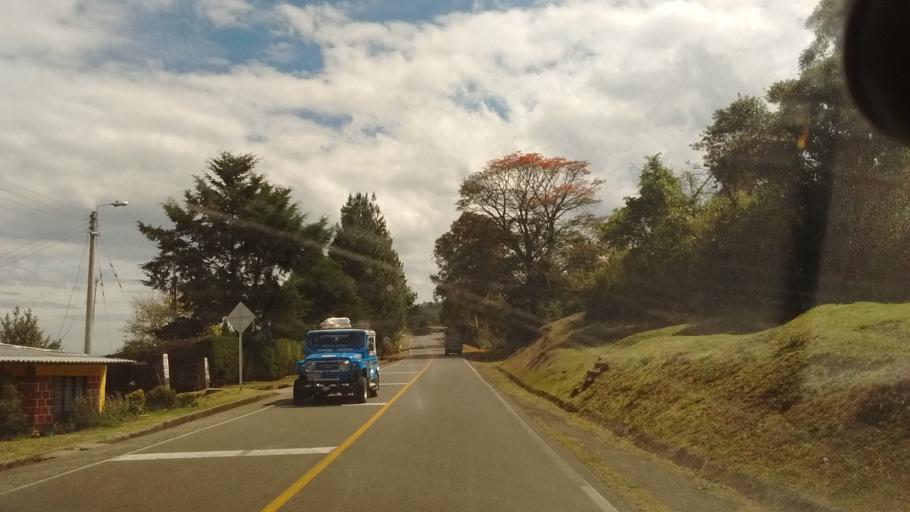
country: CO
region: Cauca
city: Cajibio
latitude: 2.6278
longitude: -76.5152
